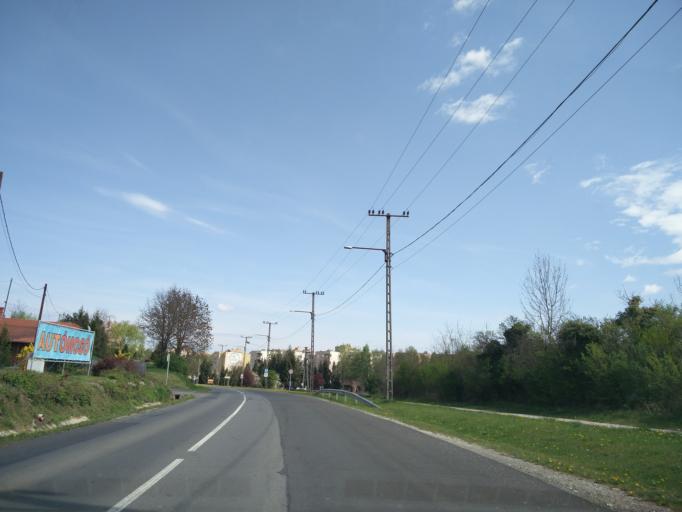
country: HU
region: Zala
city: Zalaegerszeg
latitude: 46.8198
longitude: 16.8274
